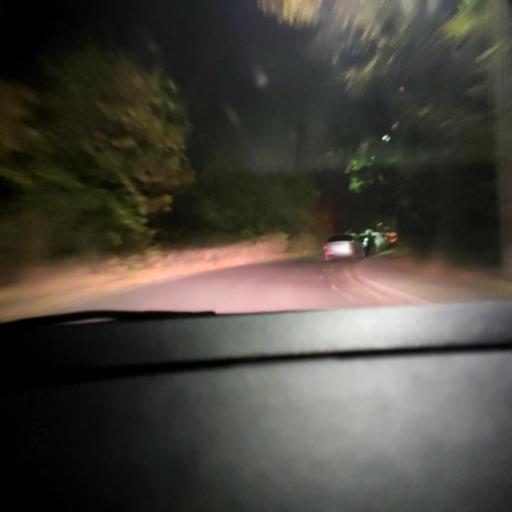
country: RU
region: Voronezj
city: Voronezh
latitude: 51.7021
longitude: 39.2238
